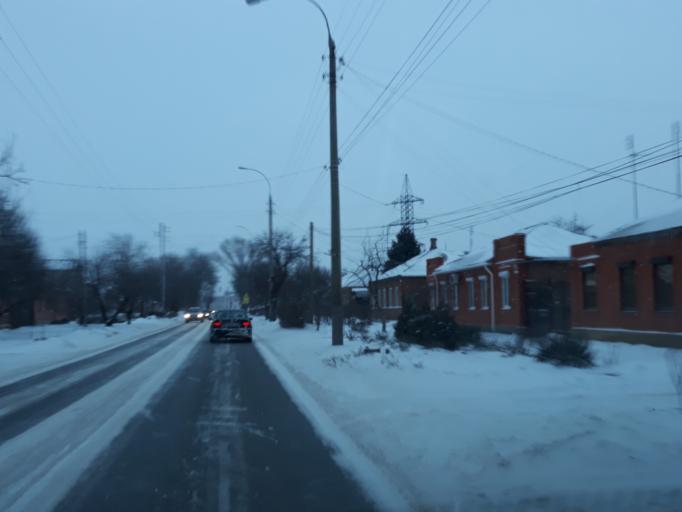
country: RU
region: Rostov
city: Taganrog
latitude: 47.2582
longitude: 38.9389
